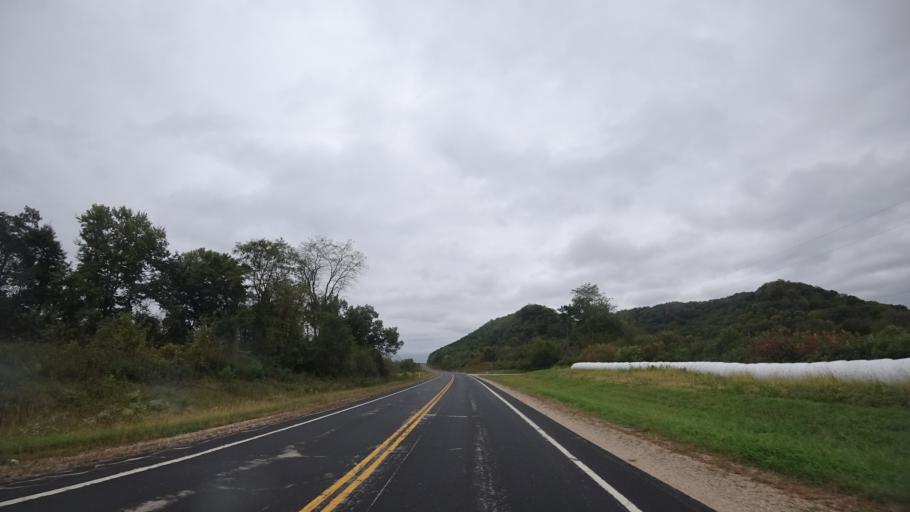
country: US
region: Wisconsin
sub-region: Grant County
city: Boscobel
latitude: 43.2029
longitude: -90.6477
